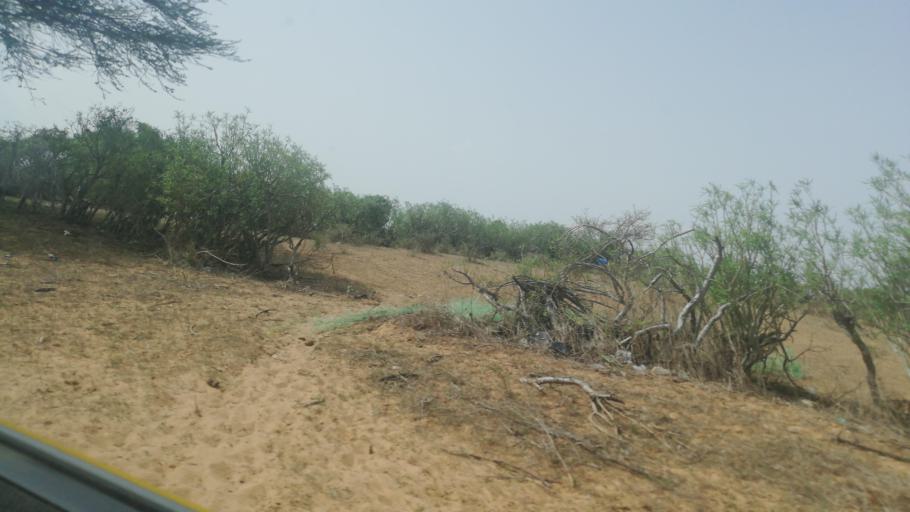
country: SN
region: Saint-Louis
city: Saint-Louis
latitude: 16.0538
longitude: -16.3346
